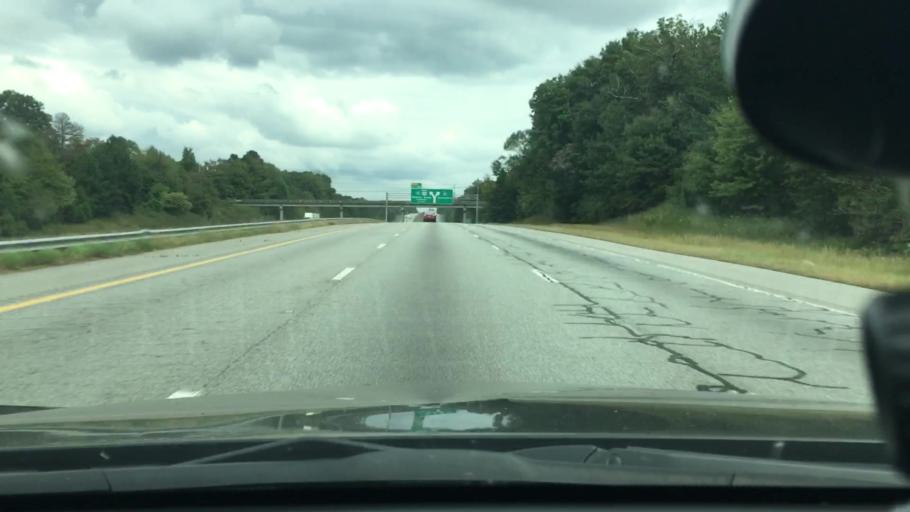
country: US
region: North Carolina
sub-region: Forsyth County
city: Clemmons
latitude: 36.0505
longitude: -80.3609
